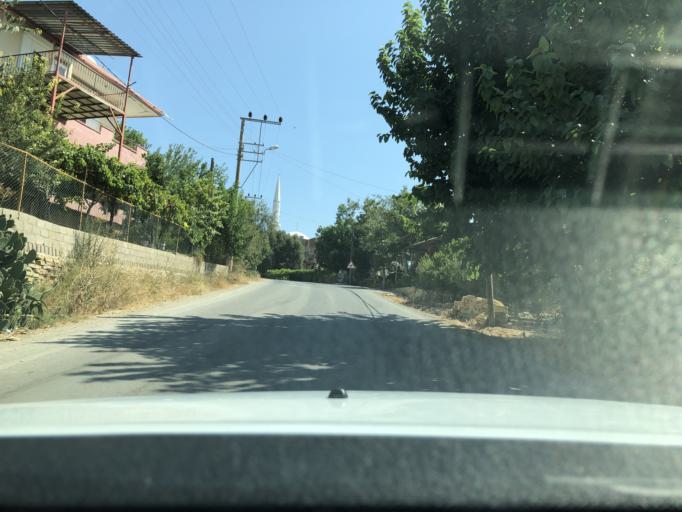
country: TR
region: Antalya
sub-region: Manavgat
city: Manavgat
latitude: 36.8120
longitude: 31.4872
